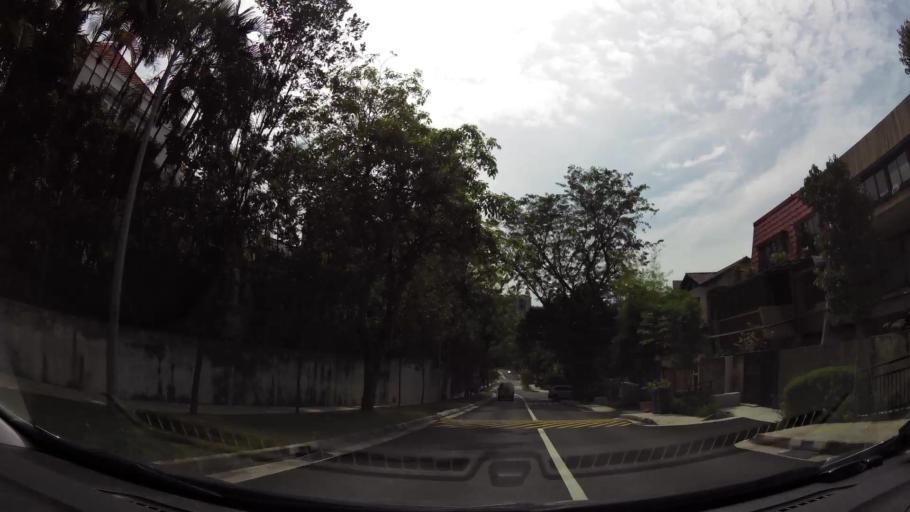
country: SG
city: Singapore
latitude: 1.3200
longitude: 103.7593
